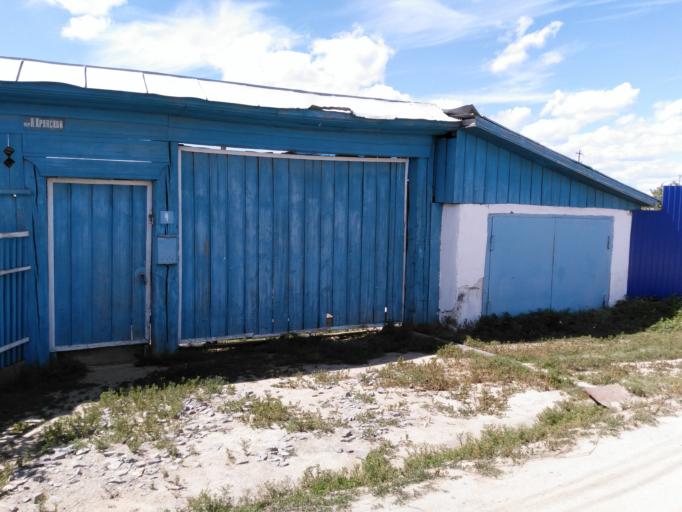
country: RU
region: Bashkortostan
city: Akhunovo
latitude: 54.2077
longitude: 59.6079
